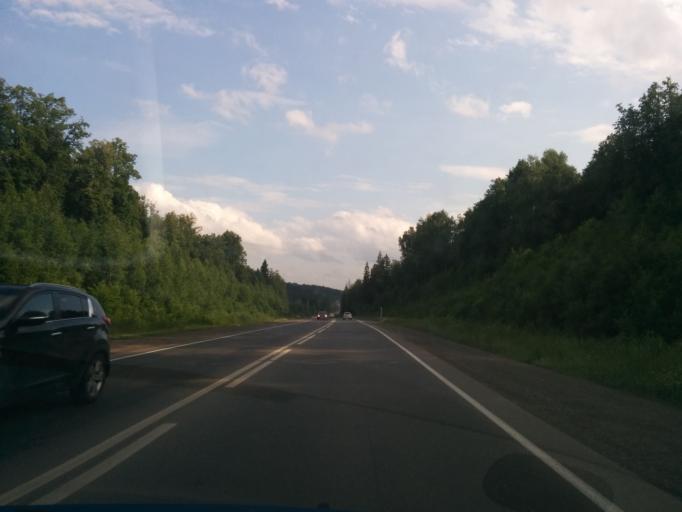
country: RU
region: Perm
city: Novyye Lyady
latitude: 58.0969
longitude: 56.4255
